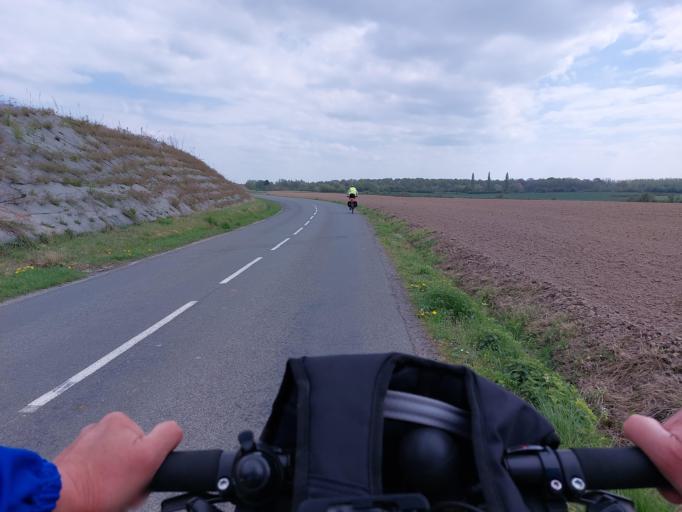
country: FR
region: Nord-Pas-de-Calais
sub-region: Departement du Nord
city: La Longueville
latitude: 50.2815
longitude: 3.8687
